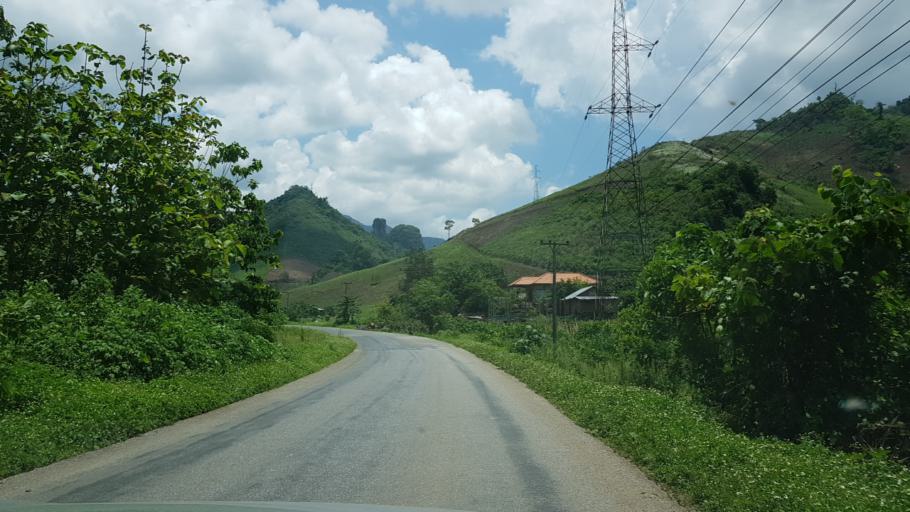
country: LA
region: Vientiane
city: Muang Kasi
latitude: 19.1334
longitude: 102.2851
